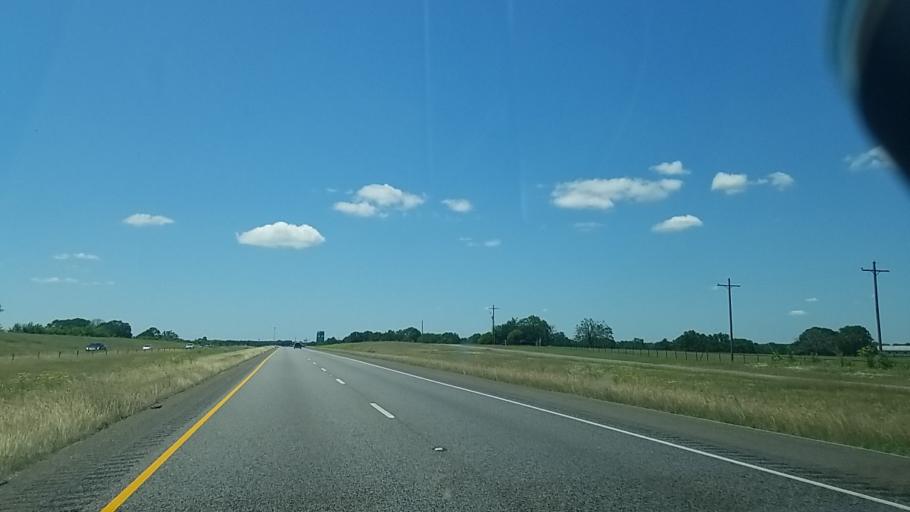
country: US
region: Texas
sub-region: Madison County
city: Madisonville
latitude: 30.9491
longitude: -95.8589
